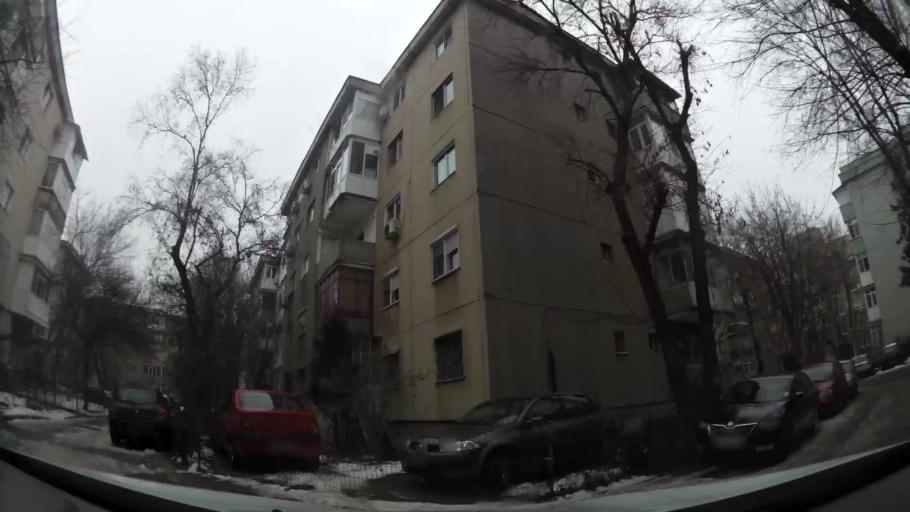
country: RO
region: Ilfov
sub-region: Comuna Chiajna
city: Rosu
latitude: 44.4384
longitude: 26.0273
